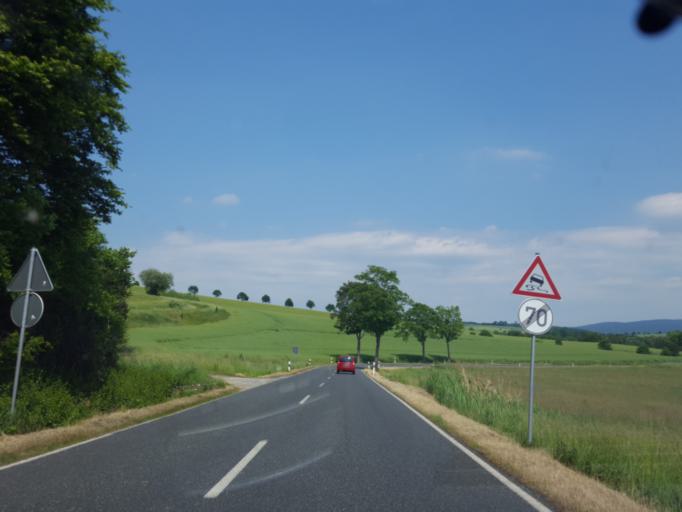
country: DE
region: Lower Saxony
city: Wulften
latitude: 51.6712
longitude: 10.1976
